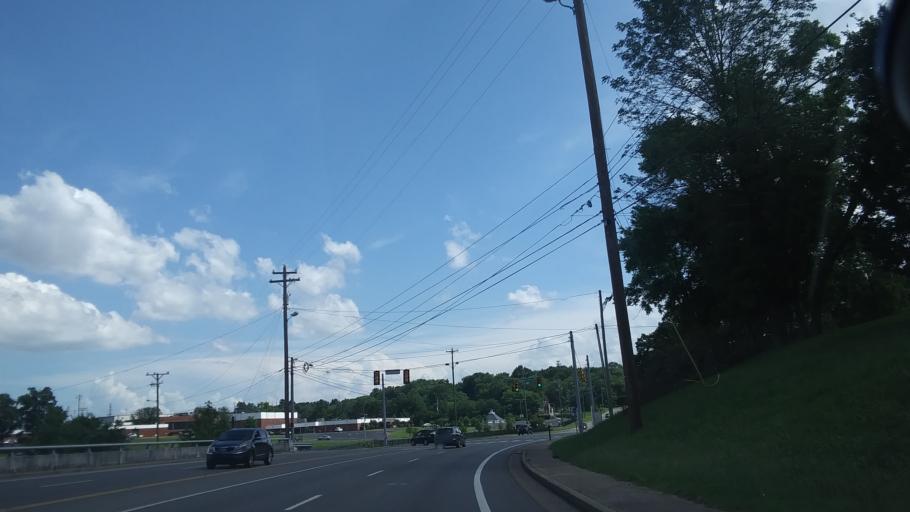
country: US
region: Tennessee
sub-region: Rutherford County
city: La Vergne
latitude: 36.0674
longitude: -86.6368
